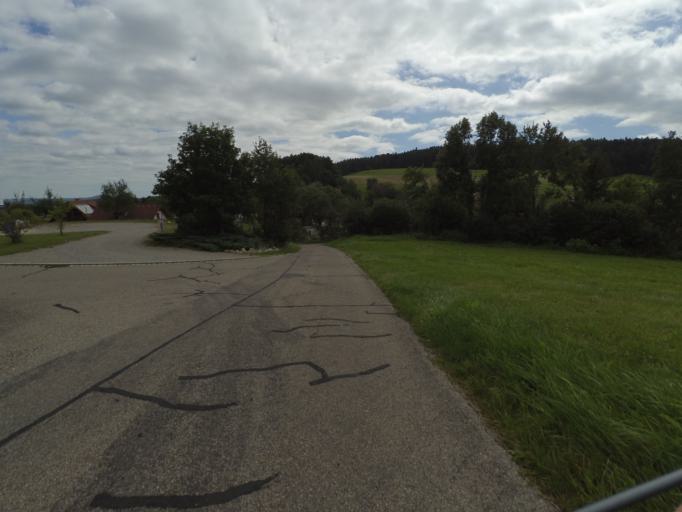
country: DE
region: Baden-Wuerttemberg
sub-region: Freiburg Region
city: Bonndorf im Schwarzwald
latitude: 47.8350
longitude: 8.3455
